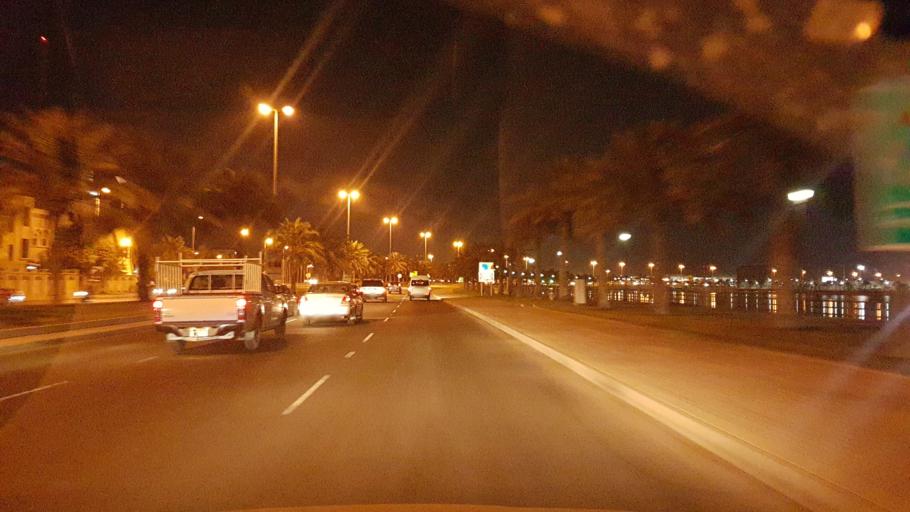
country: BH
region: Muharraq
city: Al Muharraq
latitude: 26.2530
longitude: 50.6214
